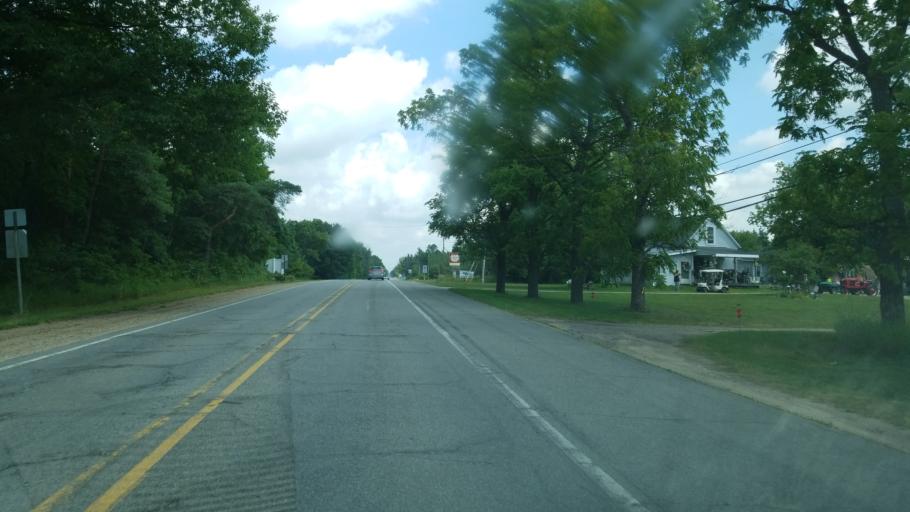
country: US
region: Michigan
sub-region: Montcalm County
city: Howard City
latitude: 43.4056
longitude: -85.4675
